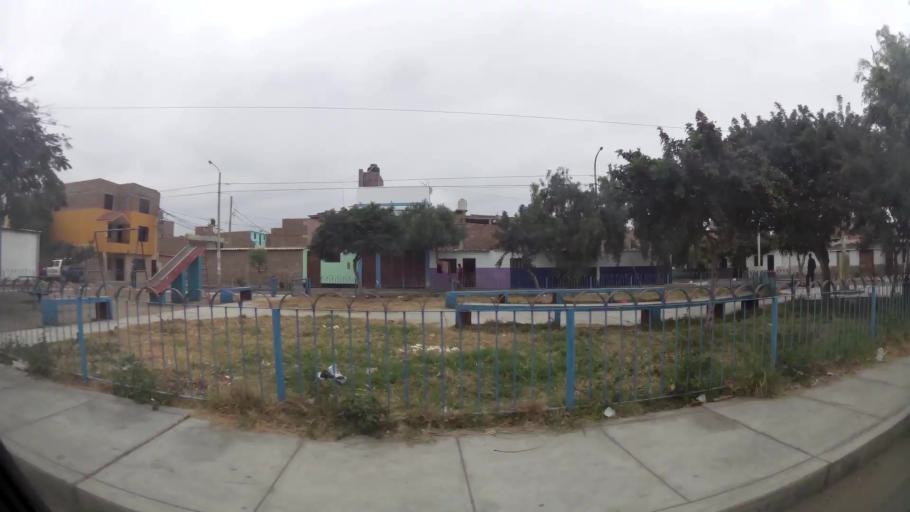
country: PE
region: La Libertad
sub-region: Provincia de Trujillo
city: Trujillo
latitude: -8.1079
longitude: -79.0400
